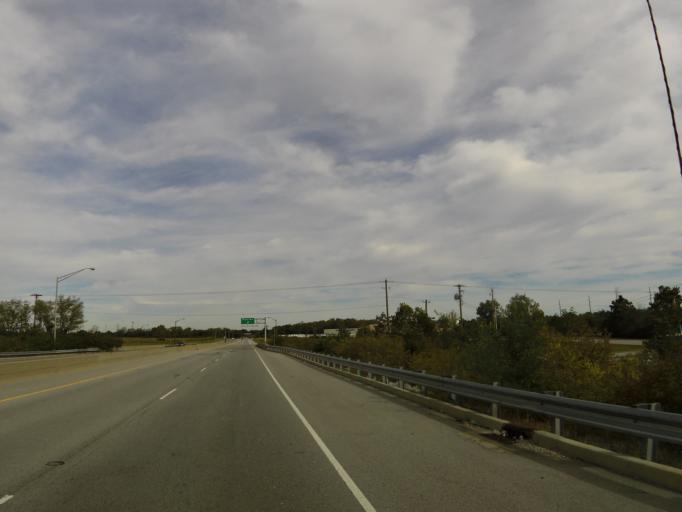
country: US
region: Indiana
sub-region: Marion County
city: Warren Park
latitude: 39.7603
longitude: -86.0426
